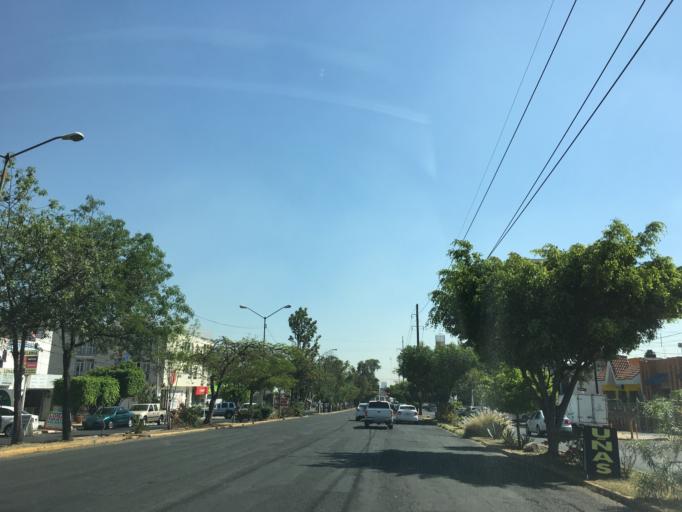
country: MX
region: Jalisco
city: Guadalajara
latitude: 20.6253
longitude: -103.4123
